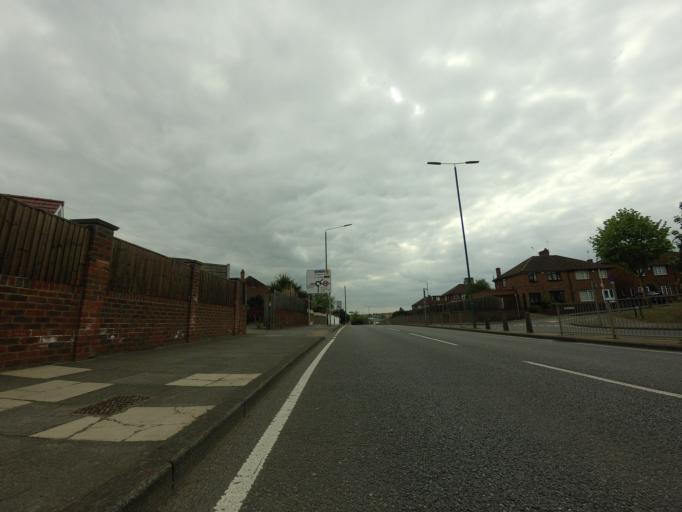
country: GB
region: England
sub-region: Greater London
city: Sidcup
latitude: 51.4162
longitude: 0.1284
